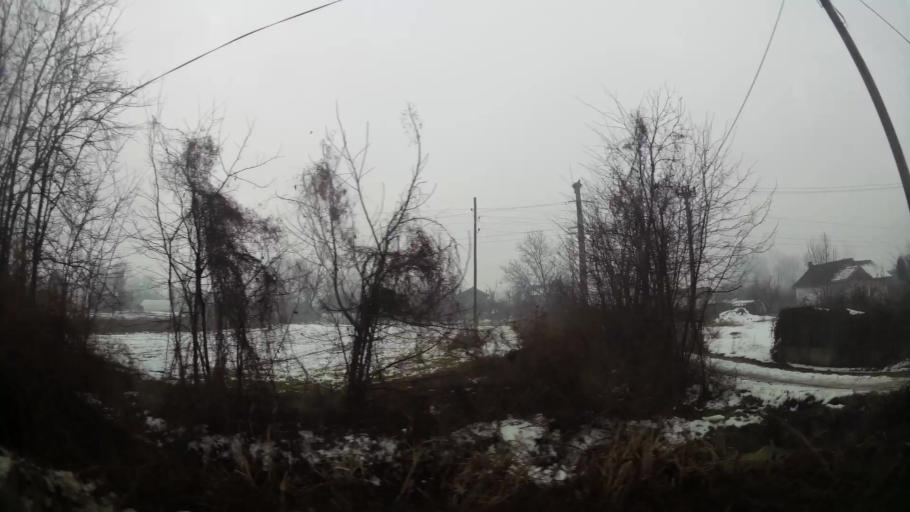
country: MK
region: Petrovec
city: Petrovec
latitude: 41.9459
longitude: 21.5971
